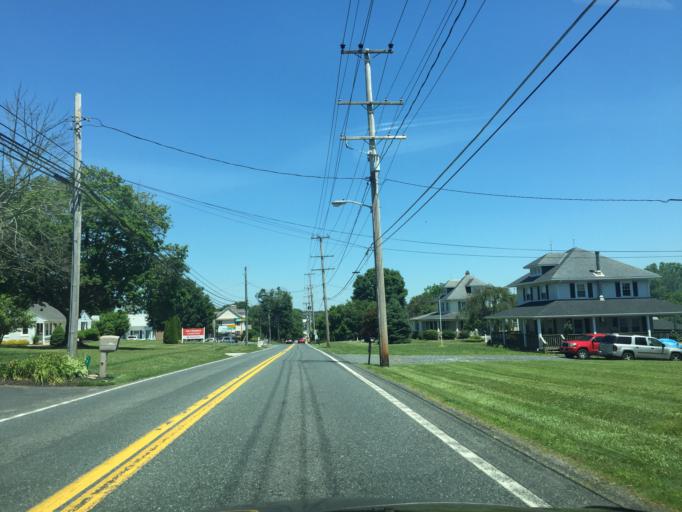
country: US
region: Maryland
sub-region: Harford County
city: Jarrettsville
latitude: 39.6007
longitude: -76.4773
